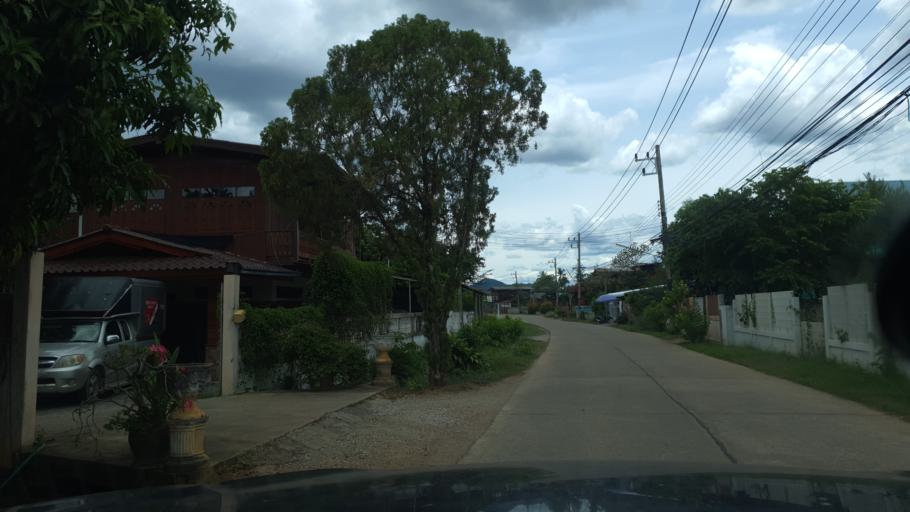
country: TH
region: Sukhothai
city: Thung Saliam
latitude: 17.3134
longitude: 99.5607
